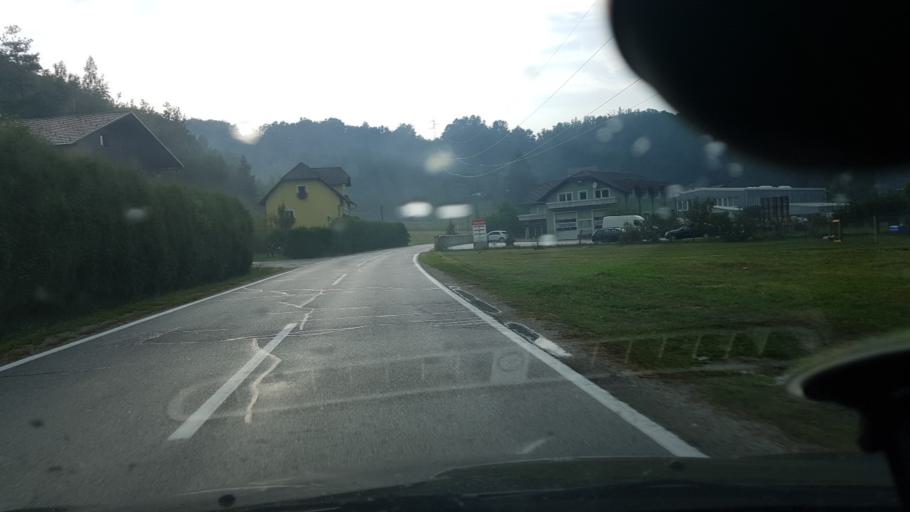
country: SI
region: Rogatec
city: Rogatec
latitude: 46.2160
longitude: 15.7284
